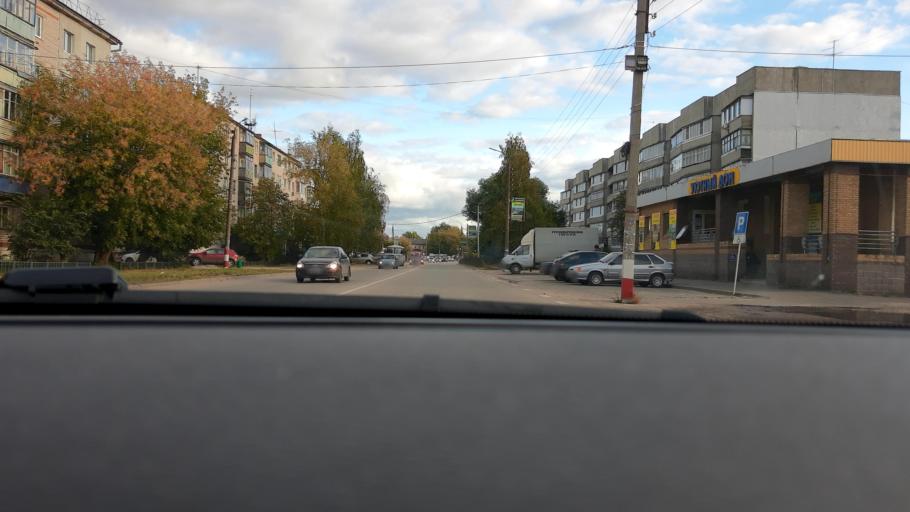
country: RU
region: Nizjnij Novgorod
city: Novaya Balakhna
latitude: 56.4971
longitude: 43.6068
